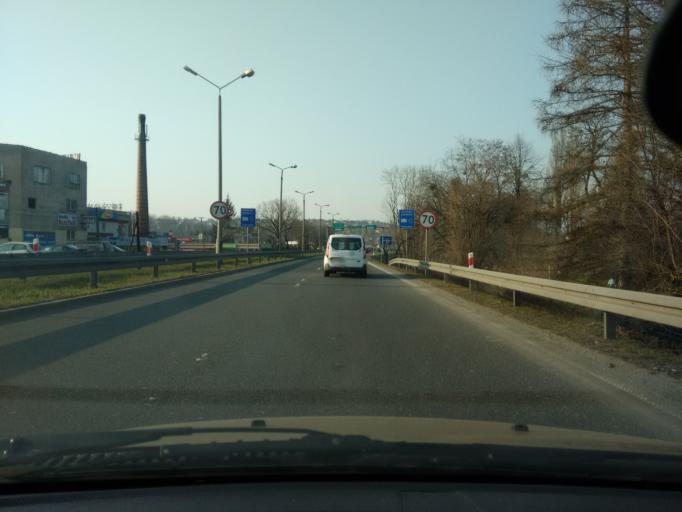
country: PL
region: Silesian Voivodeship
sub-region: Powiat cieszynski
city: Skoczow
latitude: 49.8010
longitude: 18.7918
